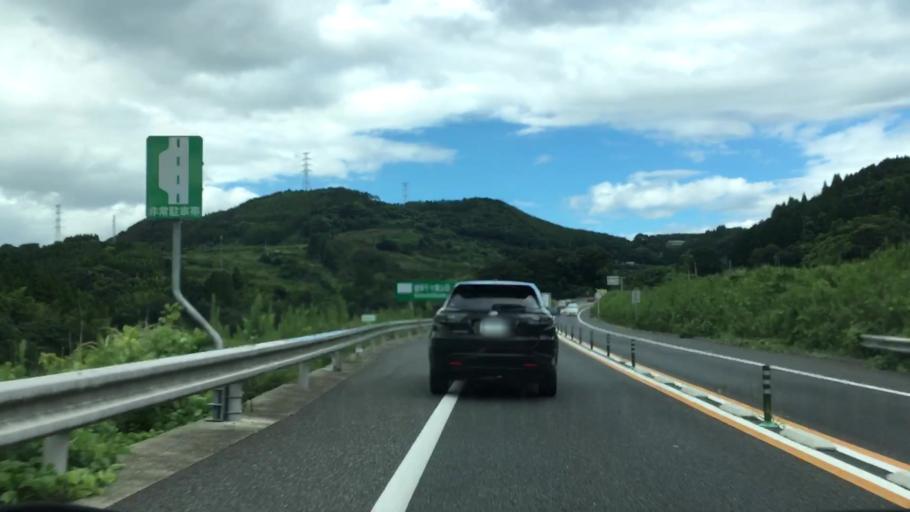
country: JP
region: Saga Prefecture
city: Karatsu
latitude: 33.3923
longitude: 129.9347
